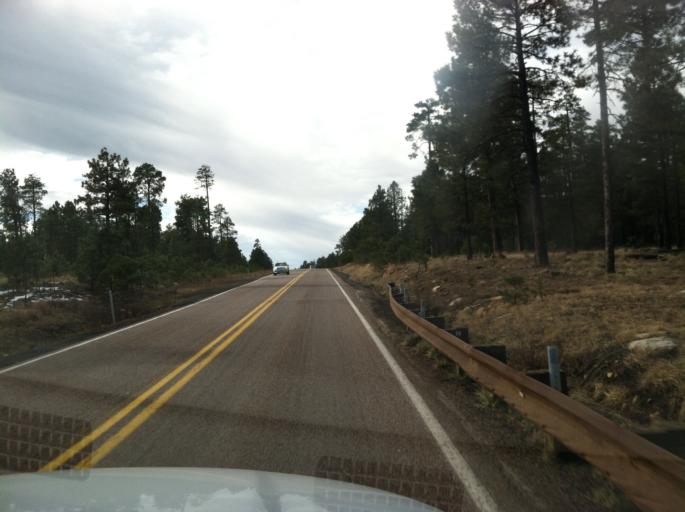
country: US
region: Arizona
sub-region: Navajo County
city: Heber-Overgaard
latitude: 34.3190
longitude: -110.8460
